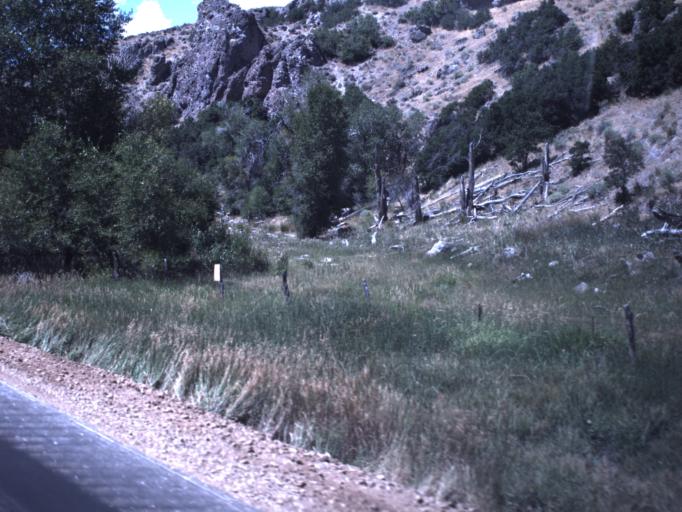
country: US
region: Utah
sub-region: Summit County
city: Francis
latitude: 40.6084
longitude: -111.3094
